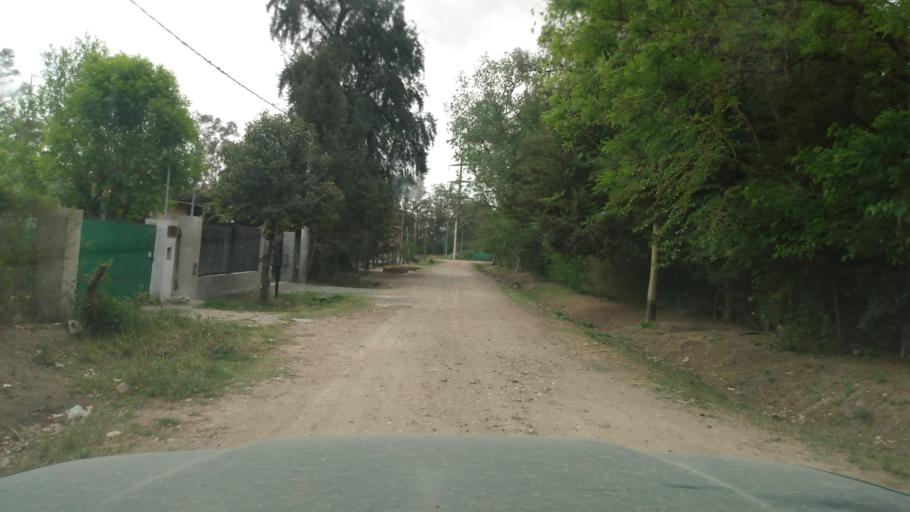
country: AR
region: Buenos Aires
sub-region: Partido de Lujan
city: Lujan
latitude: -34.5879
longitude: -59.1328
